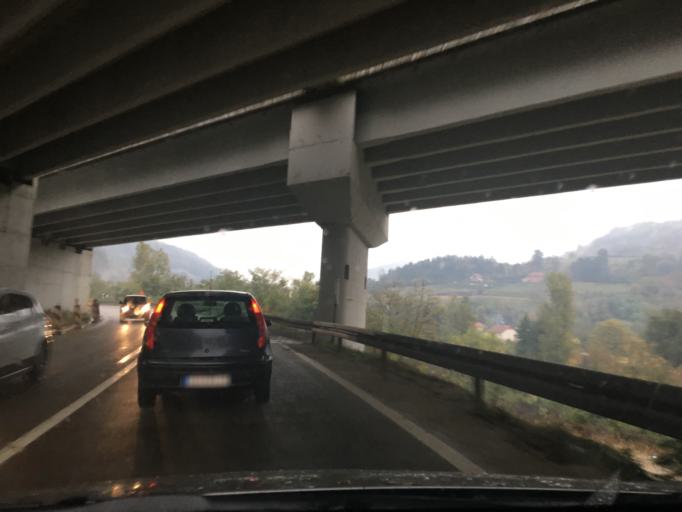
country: RS
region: Central Serbia
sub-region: Pcinjski Okrug
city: Vladicin Han
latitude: 42.7656
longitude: 22.0853
